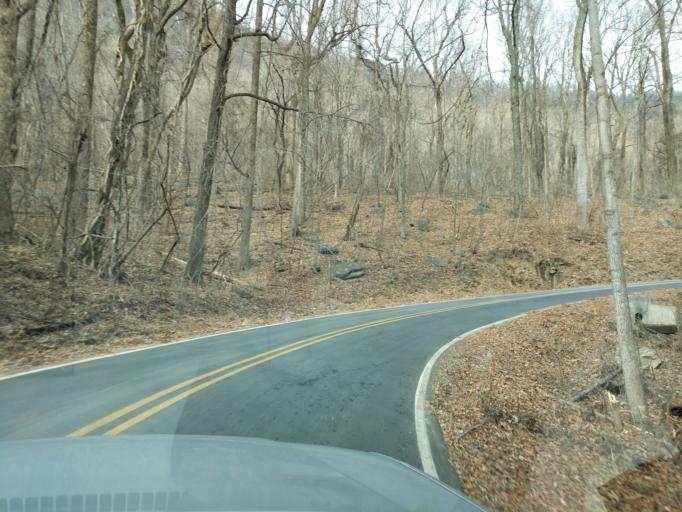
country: US
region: North Carolina
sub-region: Polk County
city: Columbus
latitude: 35.2632
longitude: -82.2363
